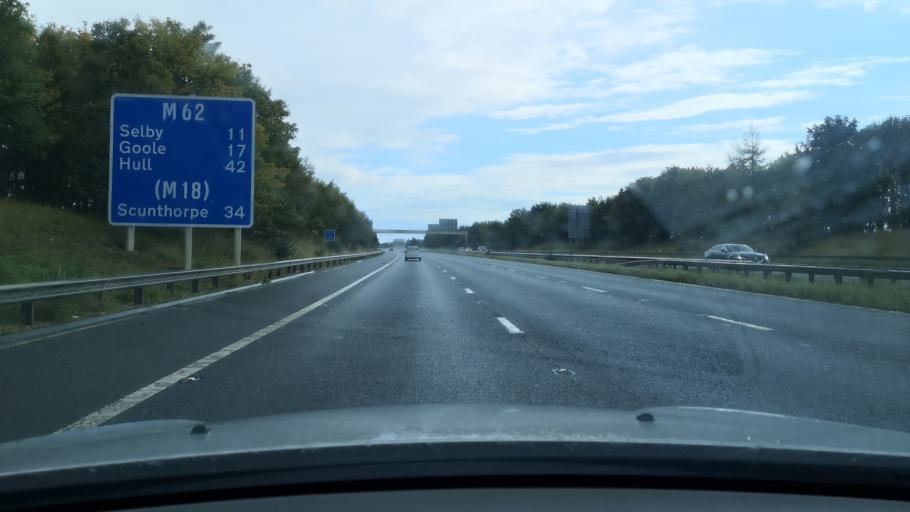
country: GB
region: England
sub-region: City and Borough of Wakefield
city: Knottingley
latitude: 53.6929
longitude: -1.2487
